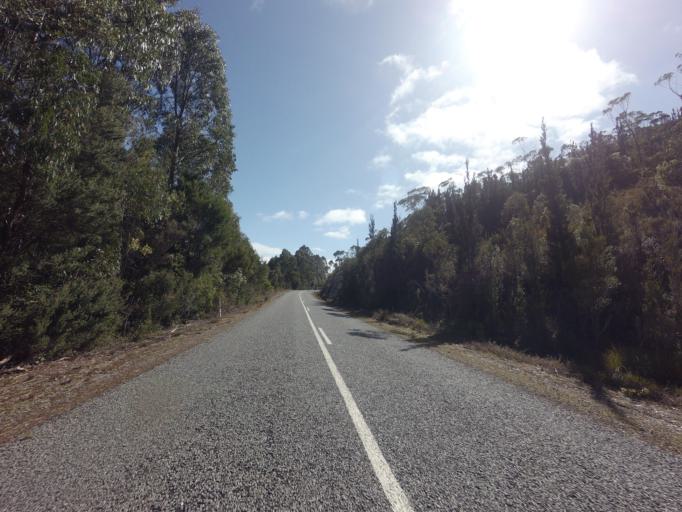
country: AU
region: Tasmania
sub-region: Huon Valley
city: Geeveston
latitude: -42.7959
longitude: 146.3948
